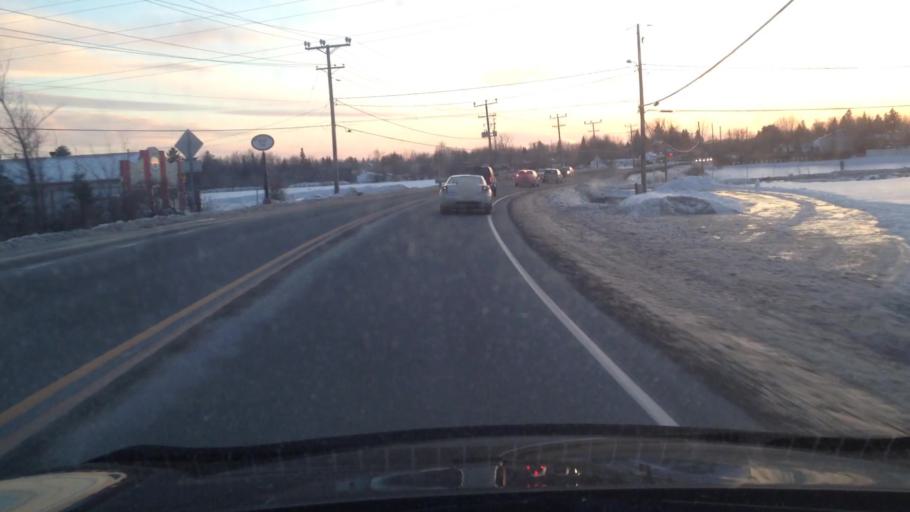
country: CA
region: Quebec
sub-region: Laurentides
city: Sainte-Sophie
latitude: 45.8265
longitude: -73.8867
